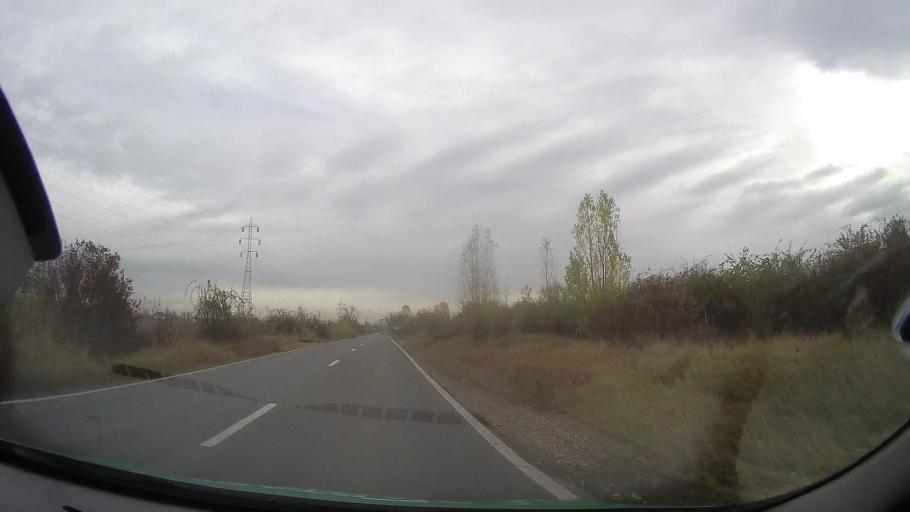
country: RO
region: Prahova
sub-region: Comuna Bucov
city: Bucov
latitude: 44.9513
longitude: 26.0929
